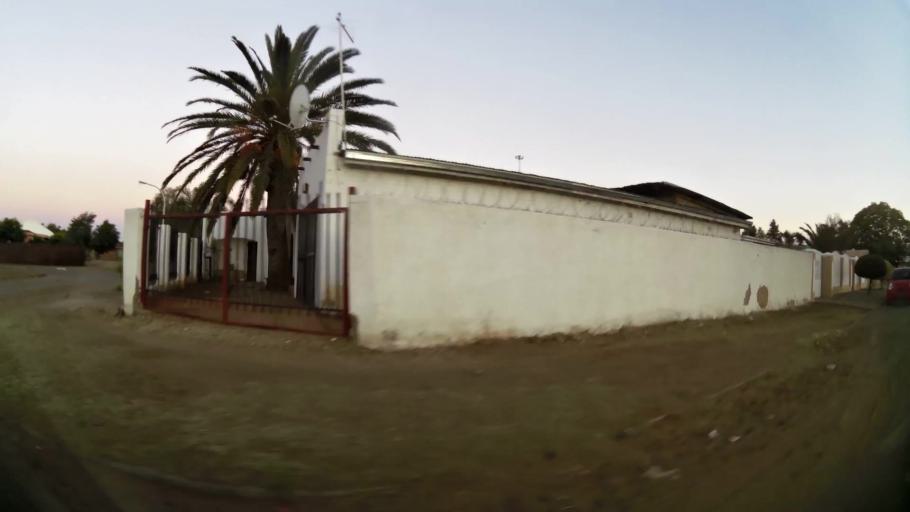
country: ZA
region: Northern Cape
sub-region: Frances Baard District Municipality
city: Kimberley
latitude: -28.7269
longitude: 24.7649
